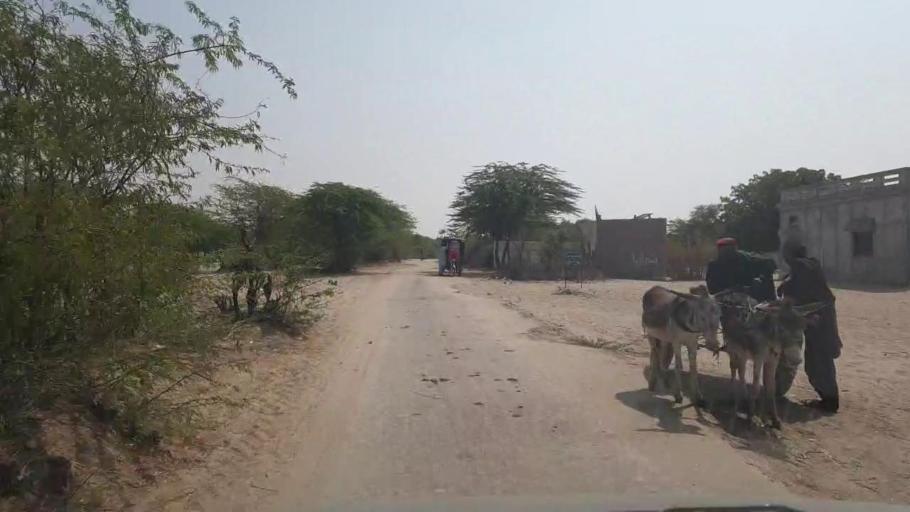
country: PK
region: Sindh
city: Chor
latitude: 25.4793
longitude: 69.7787
